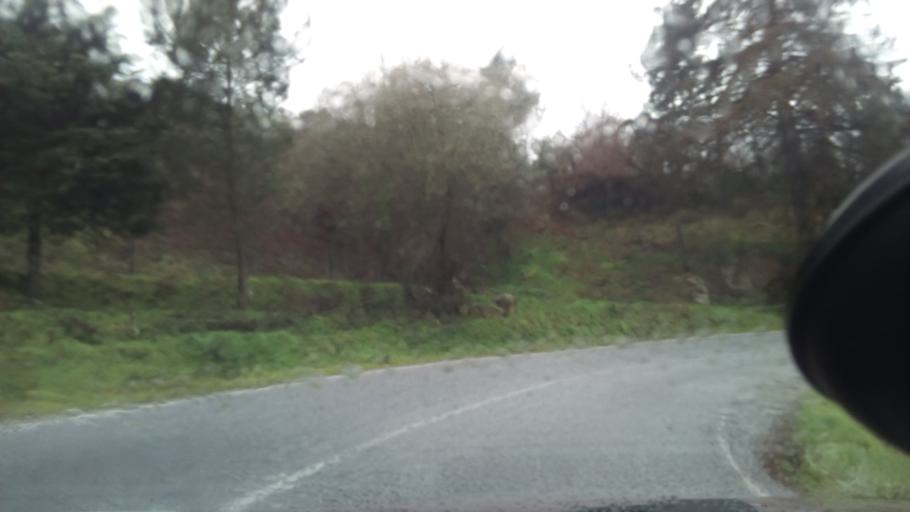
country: PT
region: Viseu
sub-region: Mangualde
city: Mangualde
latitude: 40.6325
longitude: -7.8051
